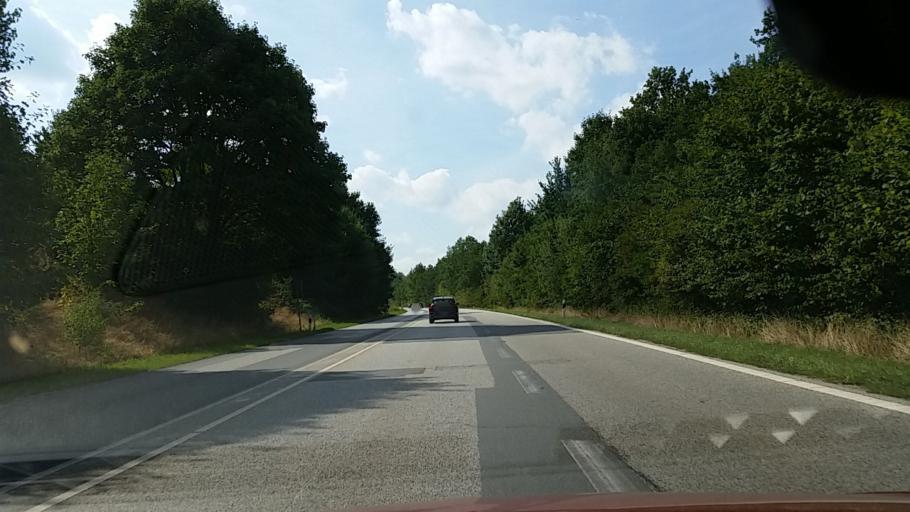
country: DE
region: Schleswig-Holstein
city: Reinbek
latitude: 53.5287
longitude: 10.2290
